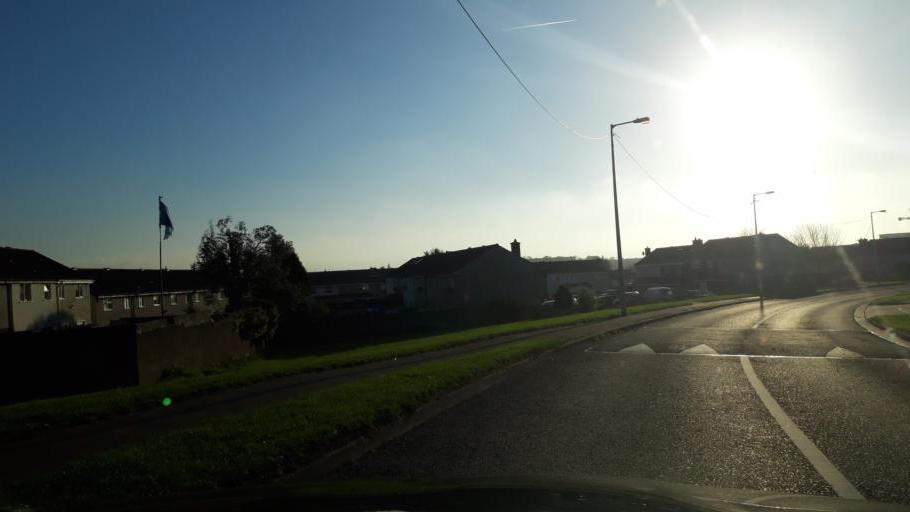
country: IE
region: Leinster
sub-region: Dublin City
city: Finglas
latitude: 53.3810
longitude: -6.3038
